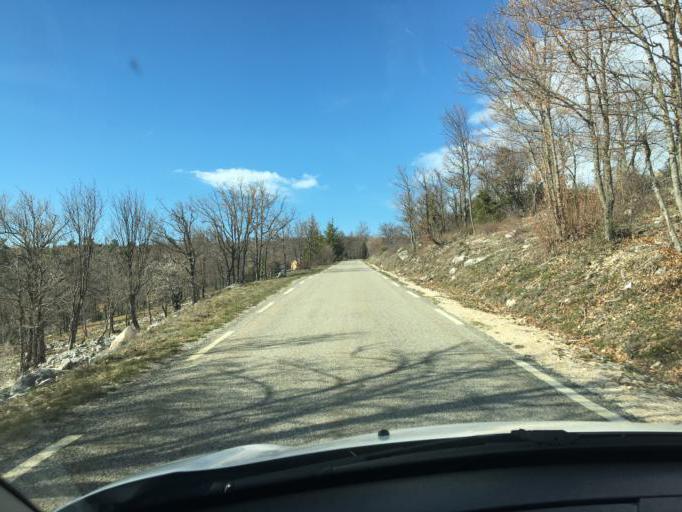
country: FR
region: Provence-Alpes-Cote d'Azur
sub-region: Departement du Vaucluse
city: Saint-Saturnin-les-Apt
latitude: 43.9708
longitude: 5.4618
